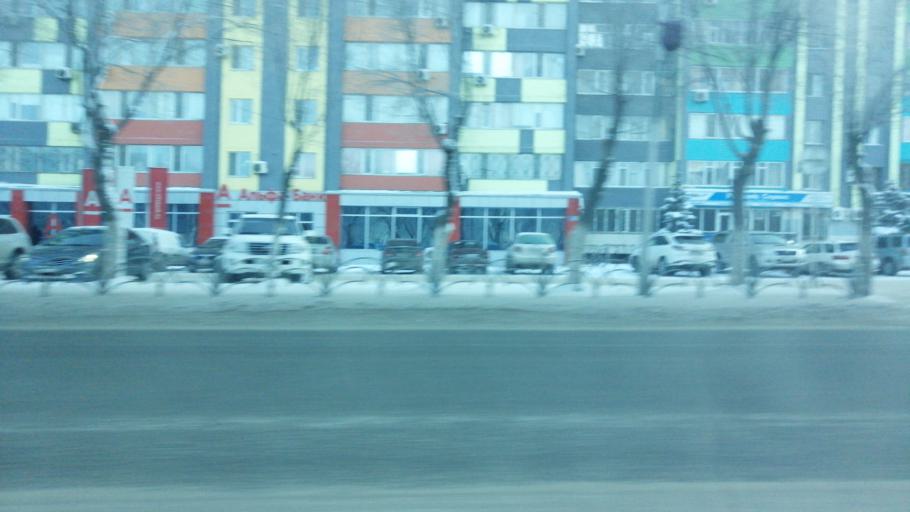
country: KZ
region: Aqtoebe
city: Aqtobe
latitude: 50.2940
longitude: 57.1738
